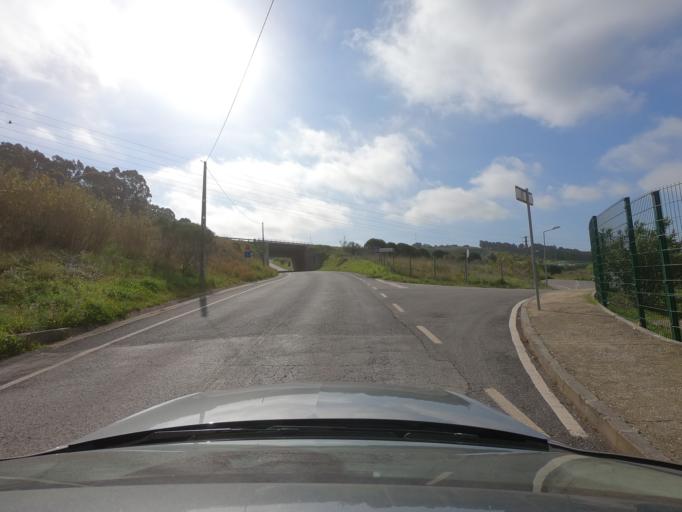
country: PT
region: Lisbon
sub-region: Oeiras
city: Barcarena
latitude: 38.7291
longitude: -9.2753
